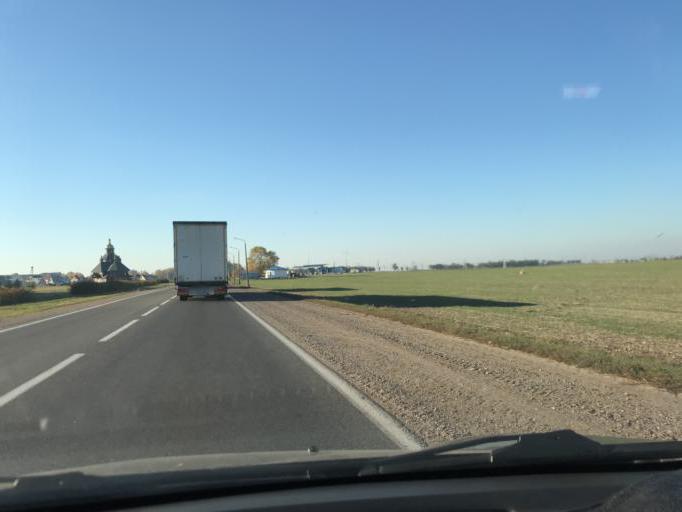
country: BY
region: Minsk
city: Slutsk
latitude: 53.0474
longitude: 27.5673
